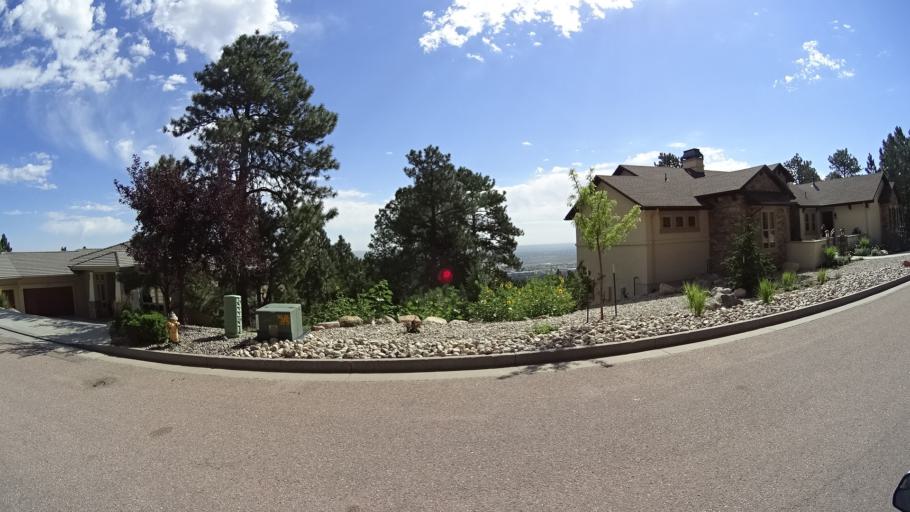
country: US
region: Colorado
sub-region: El Paso County
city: Fort Carson
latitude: 38.7481
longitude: -104.8387
